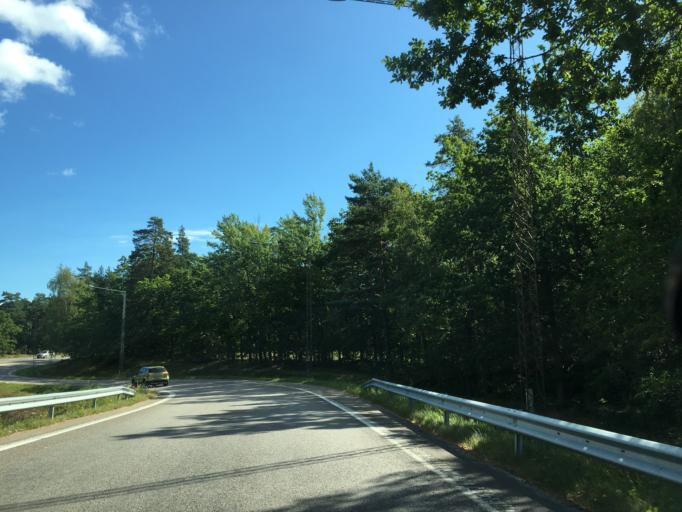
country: SE
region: Kalmar
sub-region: Kalmar Kommun
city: Kalmar
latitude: 56.6842
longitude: 16.3568
